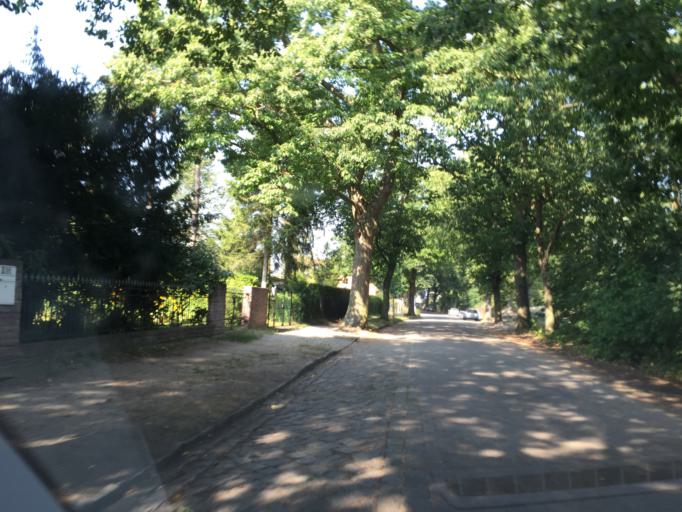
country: DE
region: Berlin
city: Rahnsdorf
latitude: 52.4358
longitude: 13.6947
